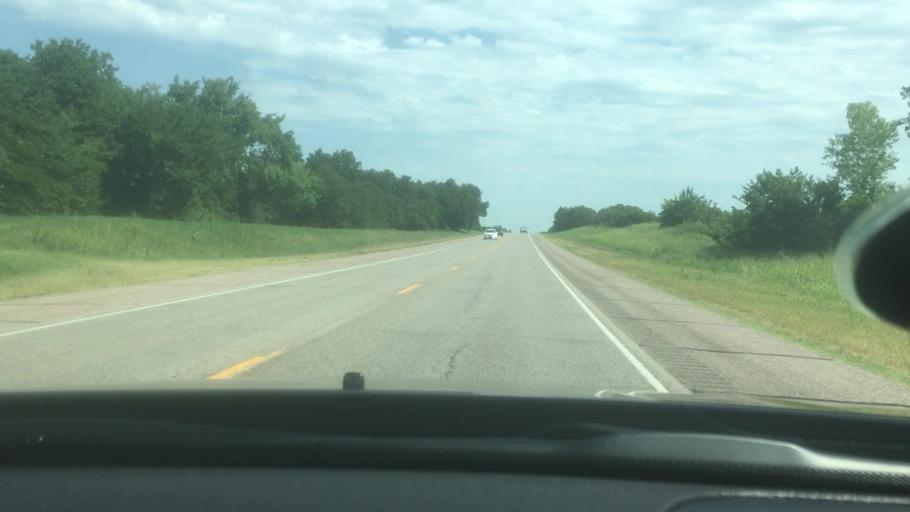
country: US
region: Oklahoma
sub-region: Seminole County
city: Konawa
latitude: 34.9967
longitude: -96.9314
